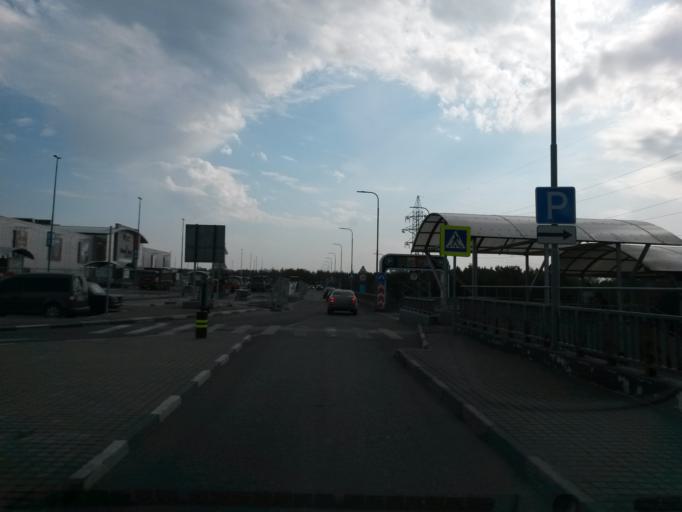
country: RU
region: Moscow
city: Tyoply Stan
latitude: 55.6033
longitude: 37.4867
